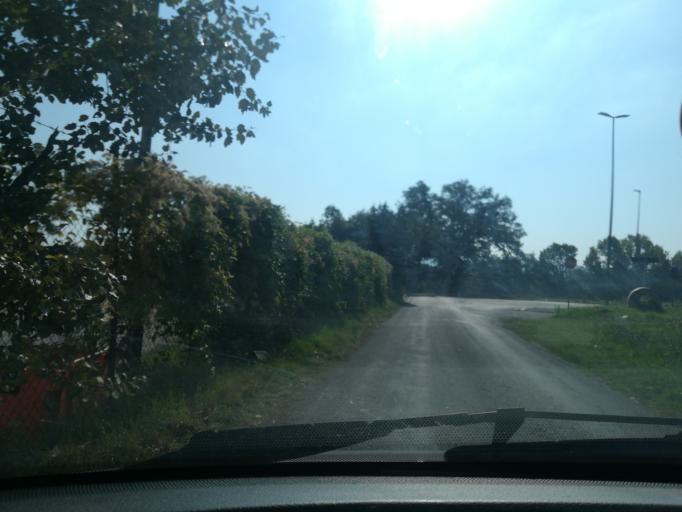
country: IT
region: The Marches
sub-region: Provincia di Macerata
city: Piediripa
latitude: 43.2719
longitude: 13.4687
